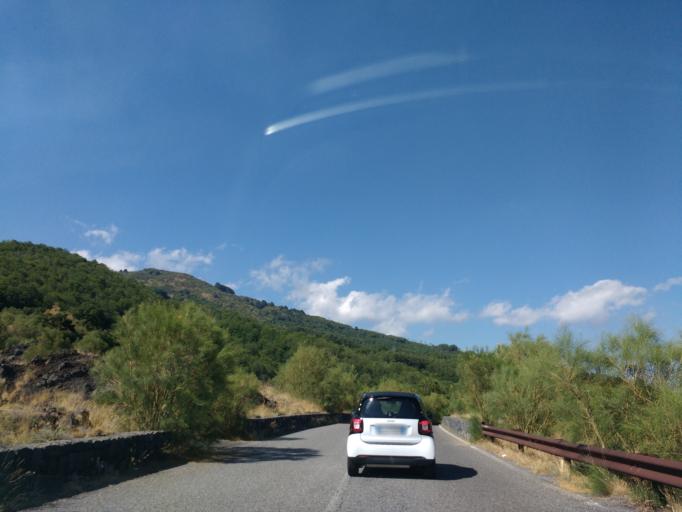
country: IT
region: Sicily
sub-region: Catania
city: Zafferana Etnea
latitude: 37.6969
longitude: 15.0573
